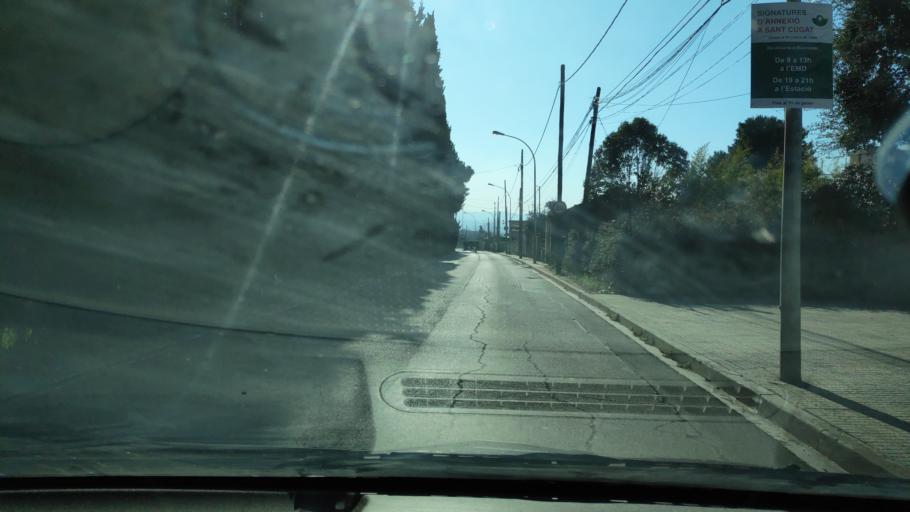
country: ES
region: Catalonia
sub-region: Provincia de Barcelona
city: Sant Cugat del Valles
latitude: 41.4941
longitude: 2.0814
